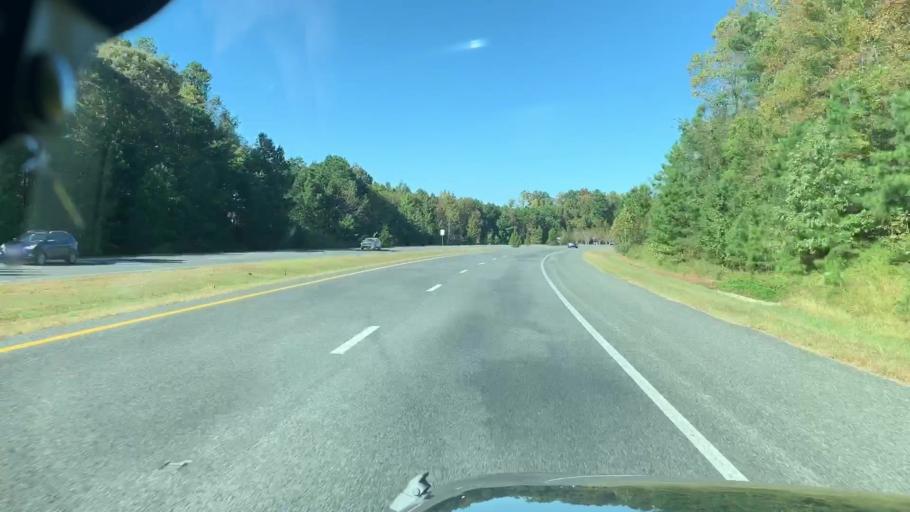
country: US
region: Virginia
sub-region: James City County
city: Williamsburg
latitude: 37.3284
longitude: -76.7557
